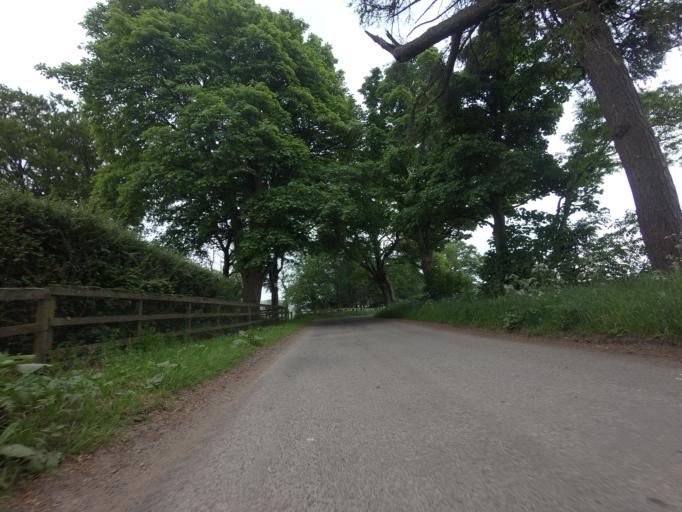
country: GB
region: Scotland
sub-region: Perth and Kinross
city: Kinross
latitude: 56.1743
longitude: -3.4401
